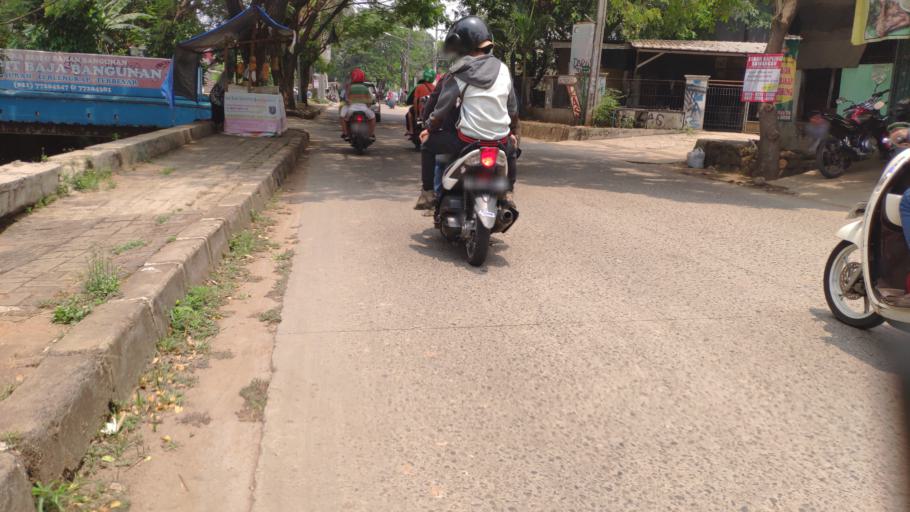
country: ID
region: West Java
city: Sawangan
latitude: -6.3879
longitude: 106.7925
